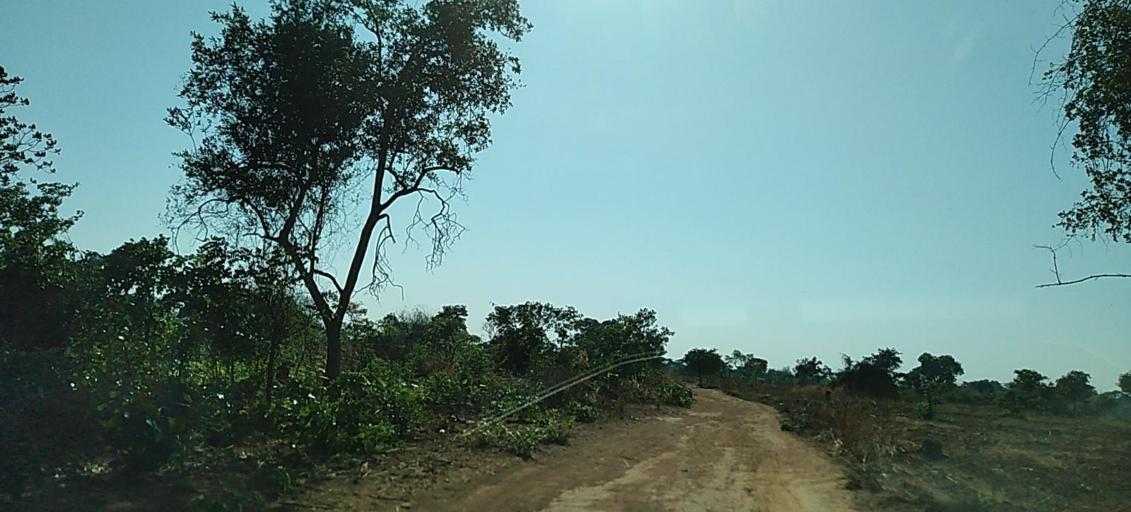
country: ZM
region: Copperbelt
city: Chililabombwe
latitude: -12.3690
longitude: 27.9075
